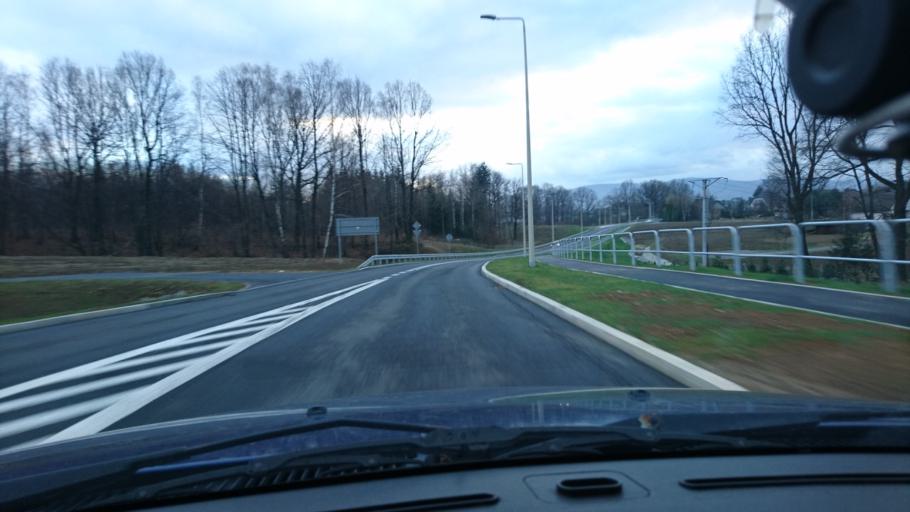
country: PL
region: Silesian Voivodeship
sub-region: Bielsko-Biala
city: Bielsko-Biala
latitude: 49.8501
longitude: 19.0703
